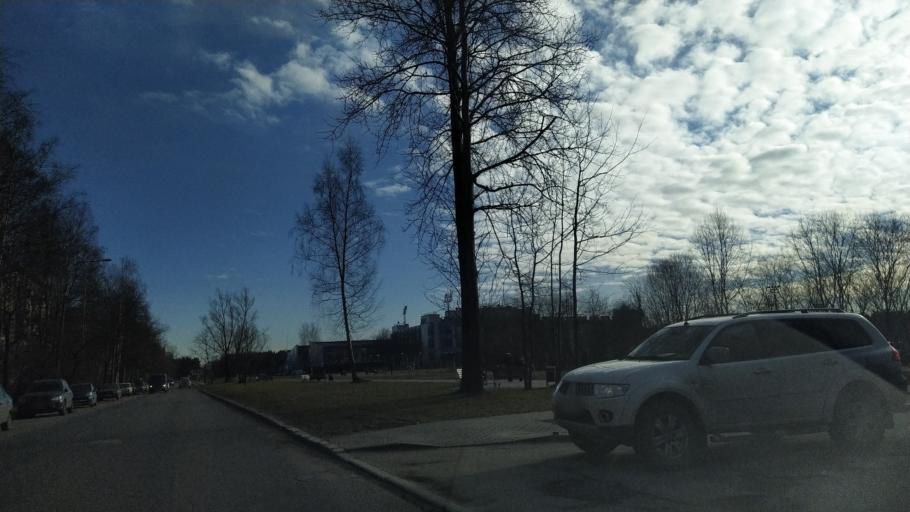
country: RU
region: Leningrad
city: Akademicheskoe
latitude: 60.0065
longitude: 30.4056
